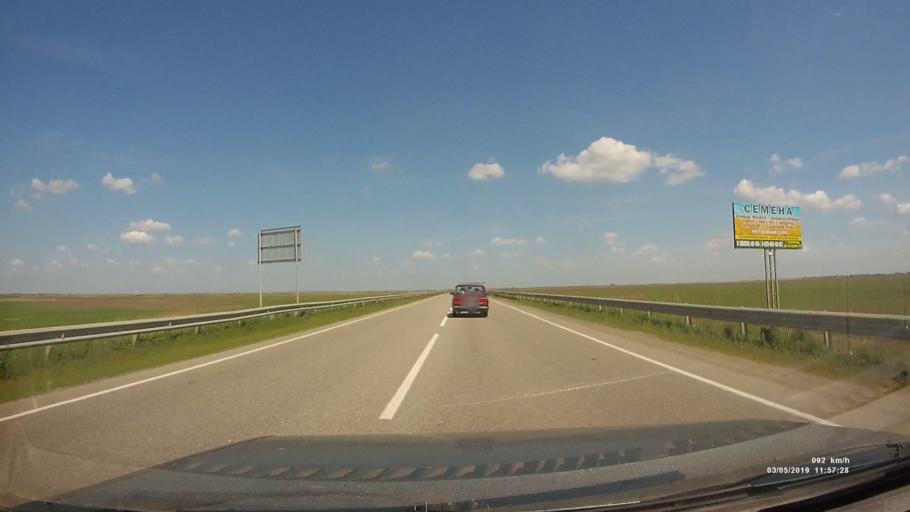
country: RU
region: Rostov
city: Bagayevskaya
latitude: 47.2069
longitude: 40.3100
